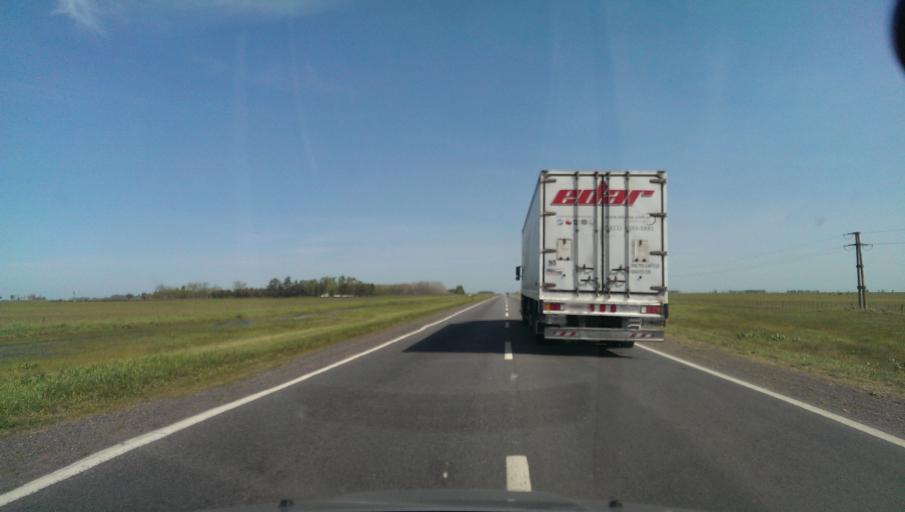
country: AR
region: Buenos Aires
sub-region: Partido de Azul
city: Azul
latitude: -36.5623
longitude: -59.6385
